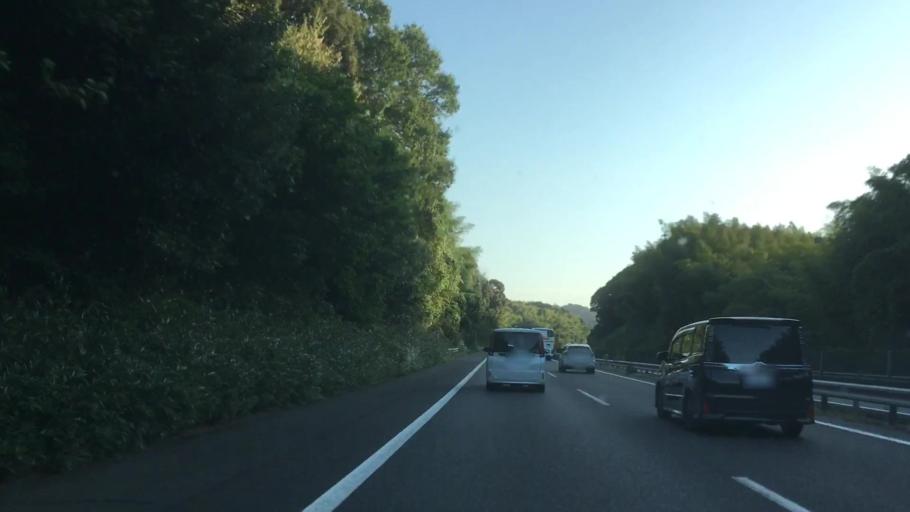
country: JP
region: Yamaguchi
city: Shimonoseki
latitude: 34.0570
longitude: 131.0073
